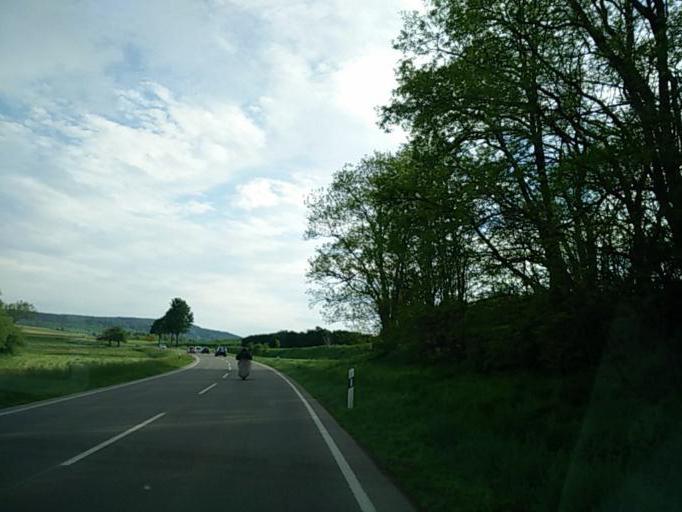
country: DE
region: Baden-Wuerttemberg
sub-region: Tuebingen Region
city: Hirrlingen
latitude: 48.4276
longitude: 8.9124
